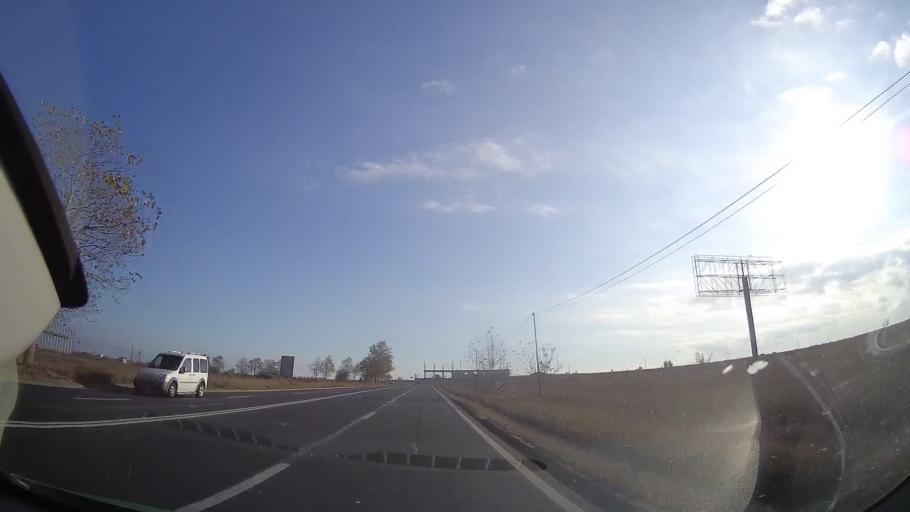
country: RO
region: Constanta
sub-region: Municipiul Mangalia
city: Mangalia
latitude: 43.7957
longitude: 28.5600
